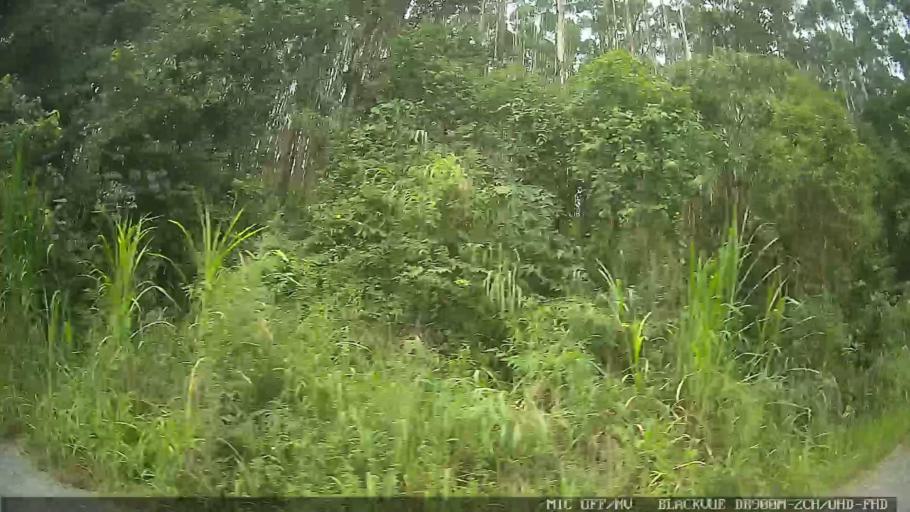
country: BR
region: Sao Paulo
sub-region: Aruja
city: Aruja
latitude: -23.4193
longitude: -46.2700
